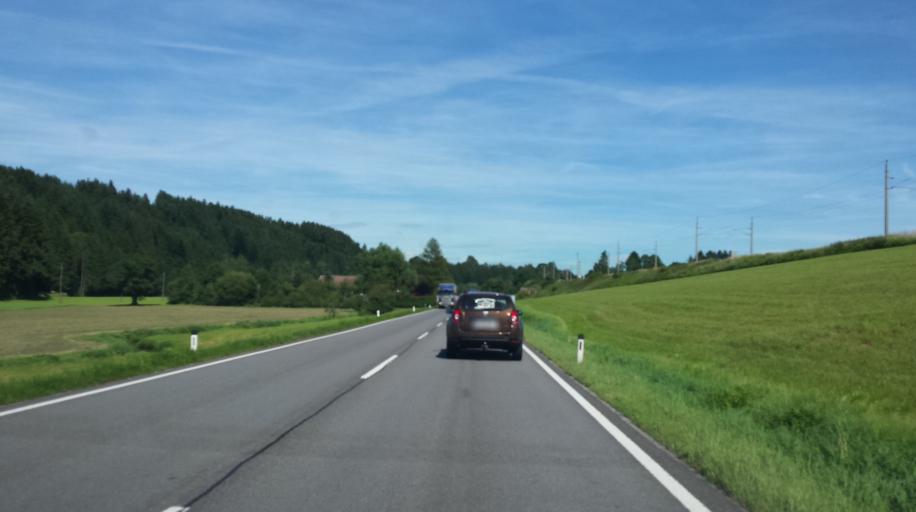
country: AT
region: Upper Austria
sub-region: Politischer Bezirk Vocklabruck
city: Frankenmarkt
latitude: 47.9872
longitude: 13.3869
